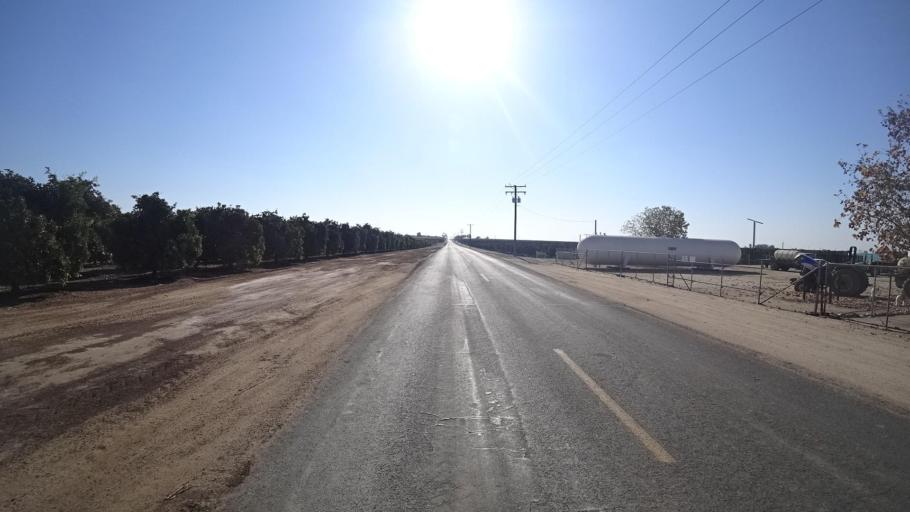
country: US
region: California
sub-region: Tulare County
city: Richgrove
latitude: 35.7232
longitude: -119.1339
